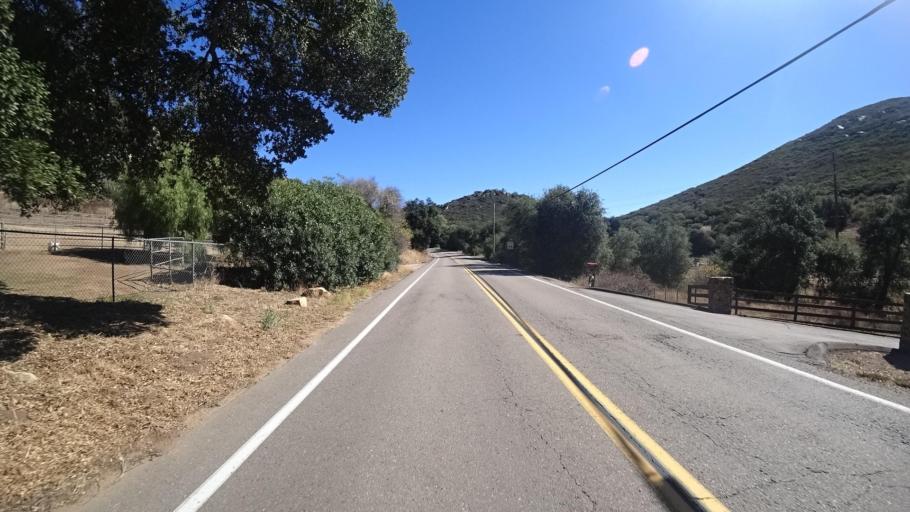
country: US
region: California
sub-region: San Diego County
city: Descanso
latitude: 32.8123
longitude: -116.6337
